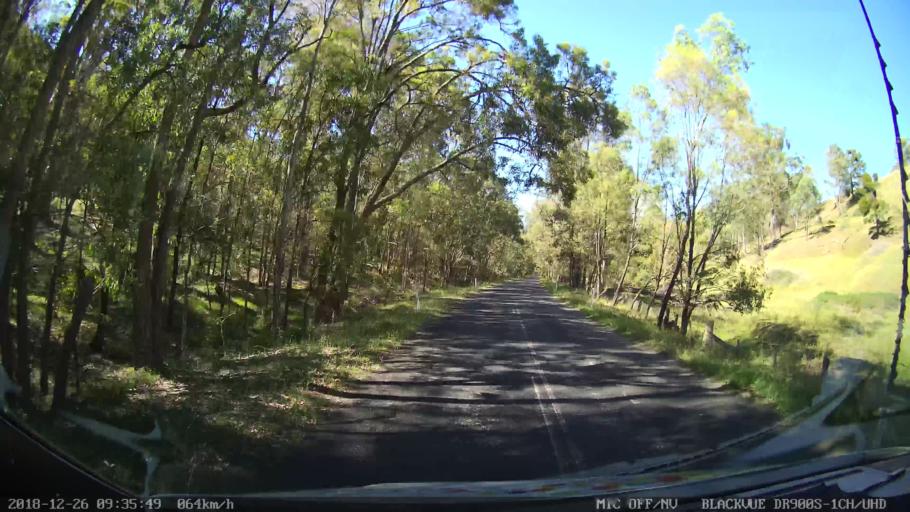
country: AU
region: New South Wales
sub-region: Mid-Western Regional
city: Kandos
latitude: -32.9183
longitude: 150.0415
